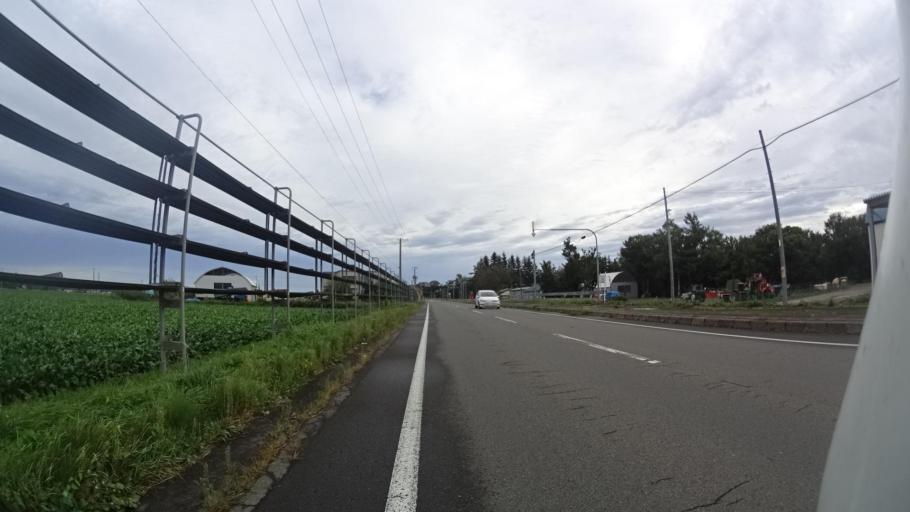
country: JP
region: Hokkaido
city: Abashiri
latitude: 43.8467
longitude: 144.5980
